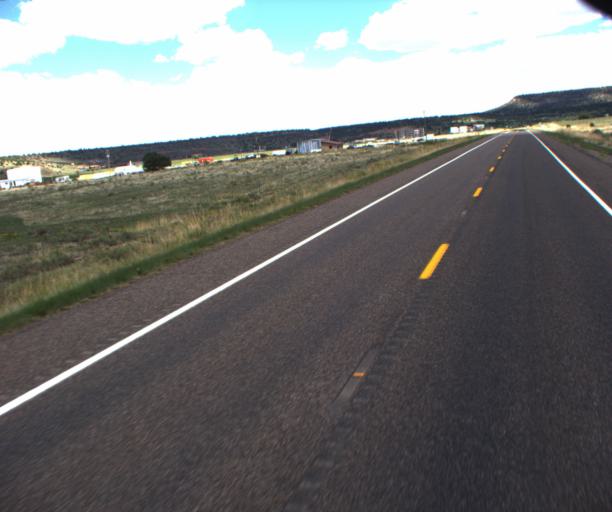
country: US
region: Arizona
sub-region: Apache County
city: Springerville
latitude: 34.1326
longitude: -109.2549
